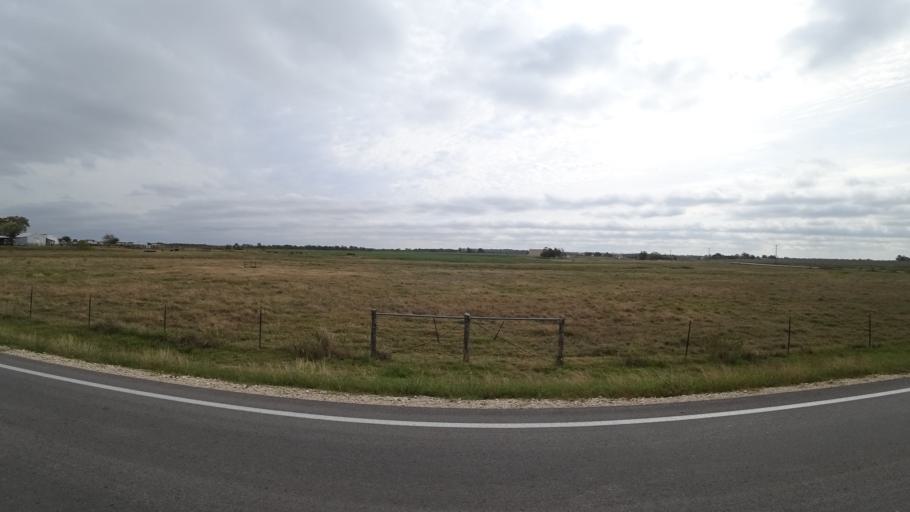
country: US
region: Texas
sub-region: Travis County
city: Manor
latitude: 30.3887
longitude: -97.5531
